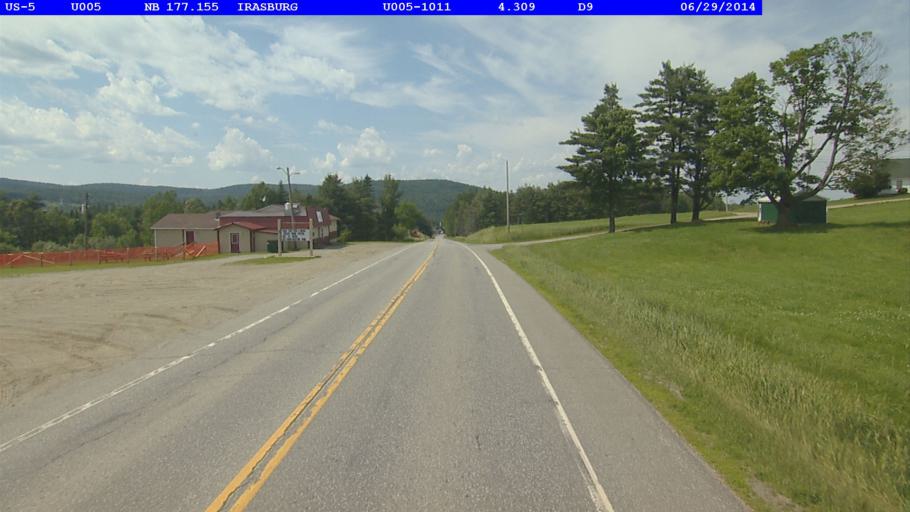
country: US
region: Vermont
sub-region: Orleans County
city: Newport
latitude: 44.8537
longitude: -72.2641
